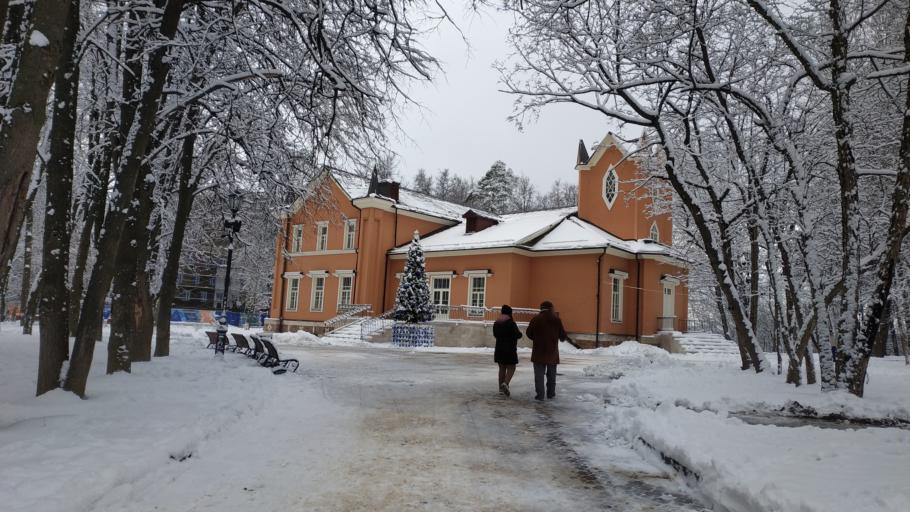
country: RU
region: Moskovskaya
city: Vidnoye
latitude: 55.5510
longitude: 37.6927
